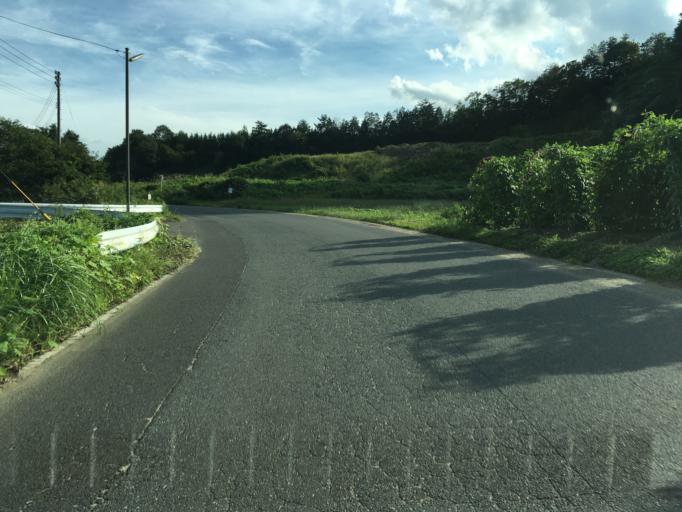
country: JP
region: Fukushima
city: Hobaramachi
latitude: 37.8056
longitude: 140.5894
